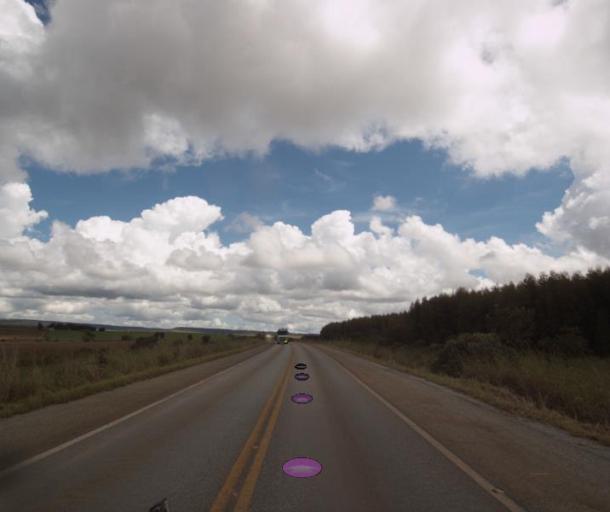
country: BR
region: Goias
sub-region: Pirenopolis
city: Pirenopolis
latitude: -15.7490
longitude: -48.6698
